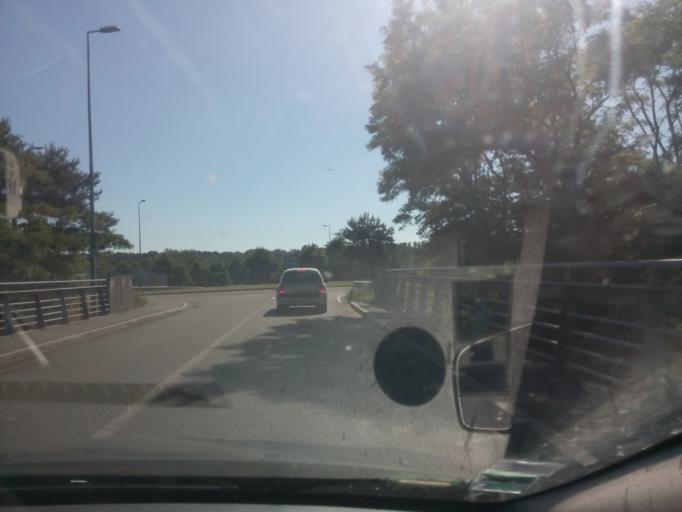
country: FR
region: Alsace
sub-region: Departement du Bas-Rhin
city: Kaltenhouse
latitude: 48.8014
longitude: 7.8351
